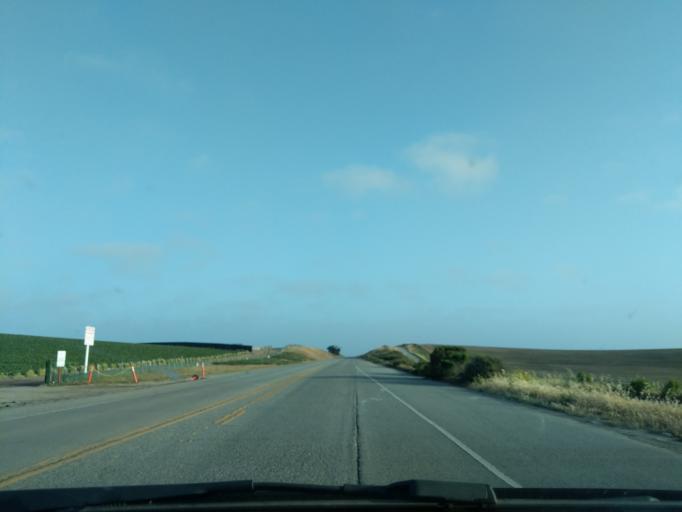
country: US
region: California
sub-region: Monterey County
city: Marina
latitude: 36.7201
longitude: -121.7877
